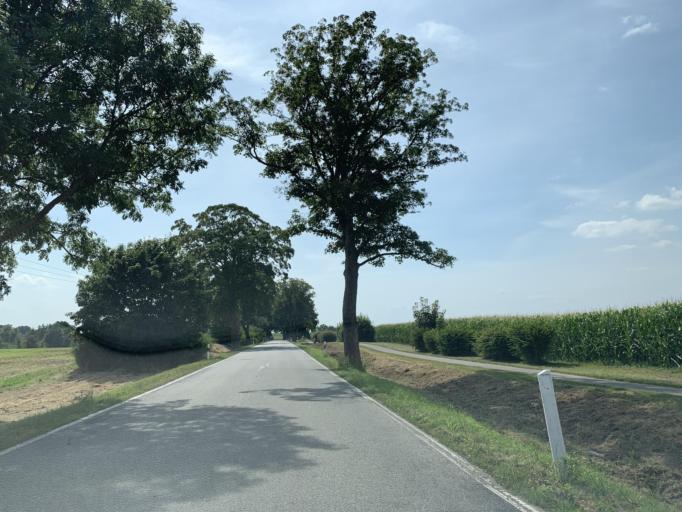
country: DE
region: Mecklenburg-Vorpommern
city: Neverin
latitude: 53.6128
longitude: 13.3309
